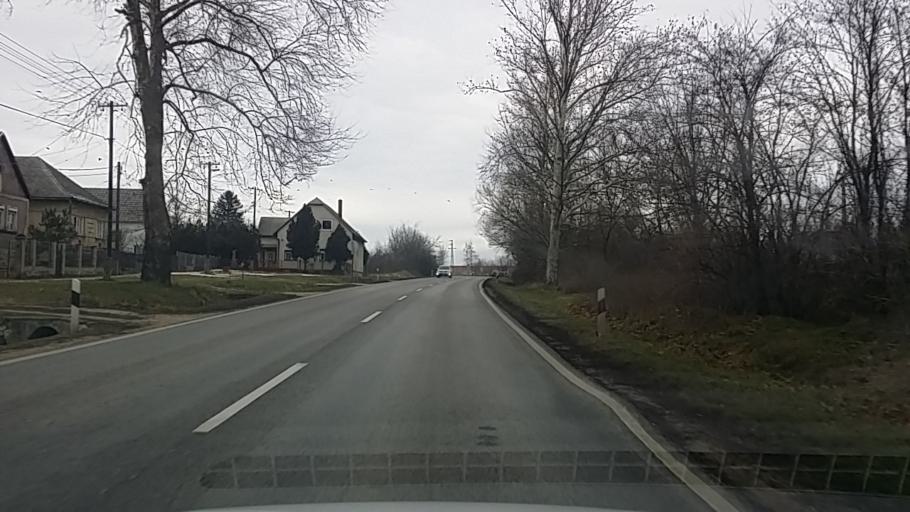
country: HU
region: Fejer
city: Mor
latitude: 47.3704
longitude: 18.1947
